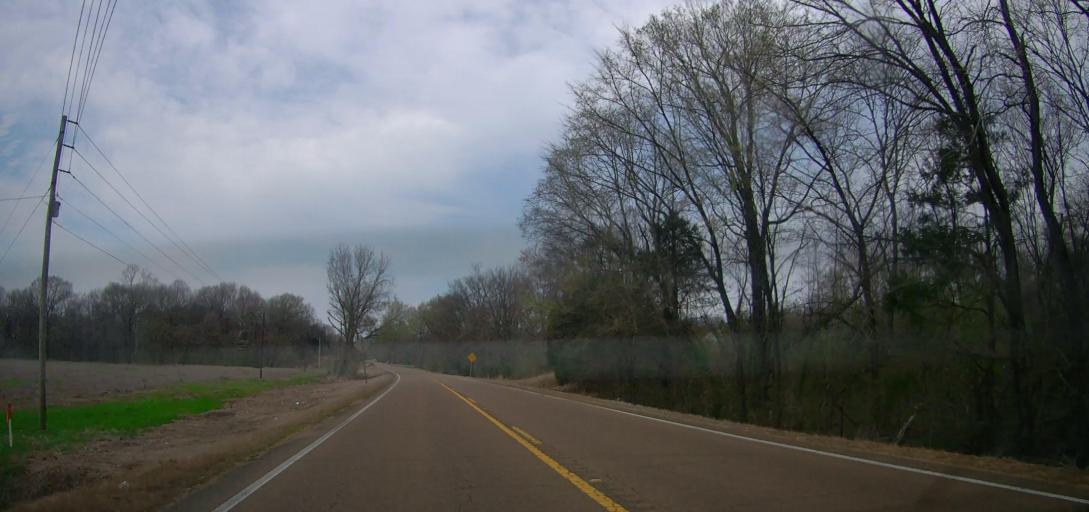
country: US
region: Mississippi
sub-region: Marshall County
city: Byhalia
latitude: 34.8468
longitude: -89.6197
